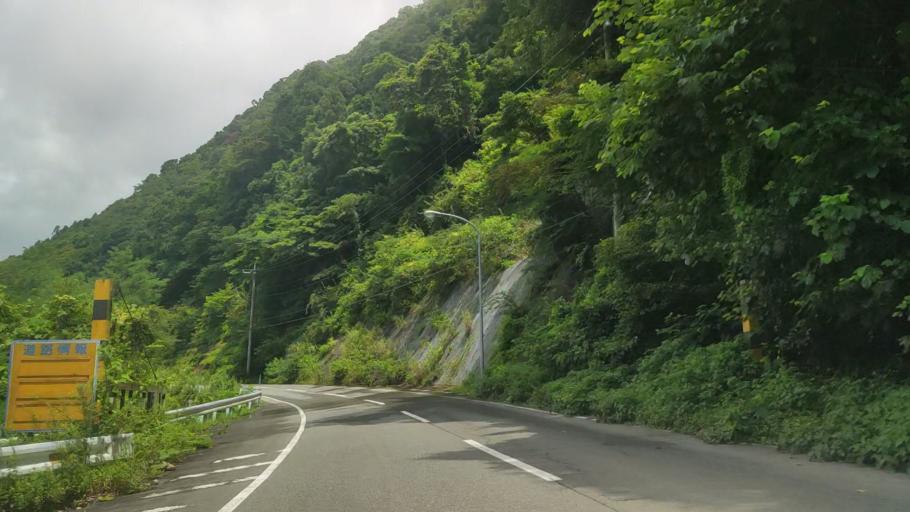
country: JP
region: Shizuoka
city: Fujinomiya
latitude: 35.2404
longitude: 138.5108
